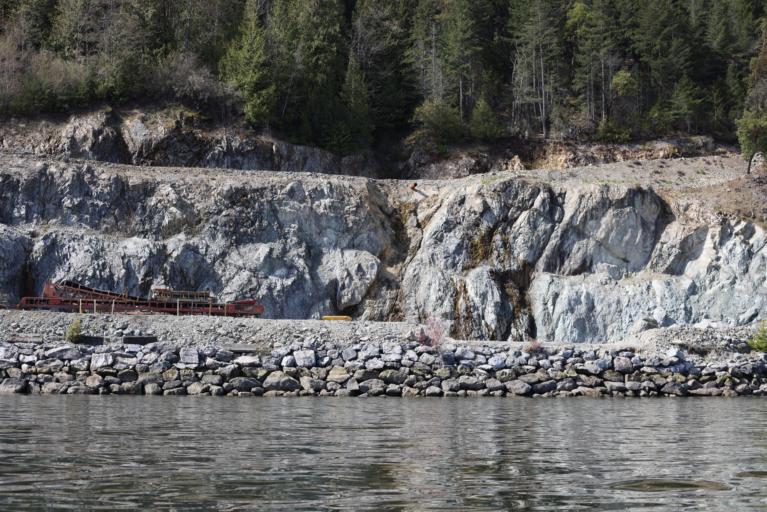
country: CA
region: British Columbia
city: North Saanich
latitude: 48.5824
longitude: -123.5202
